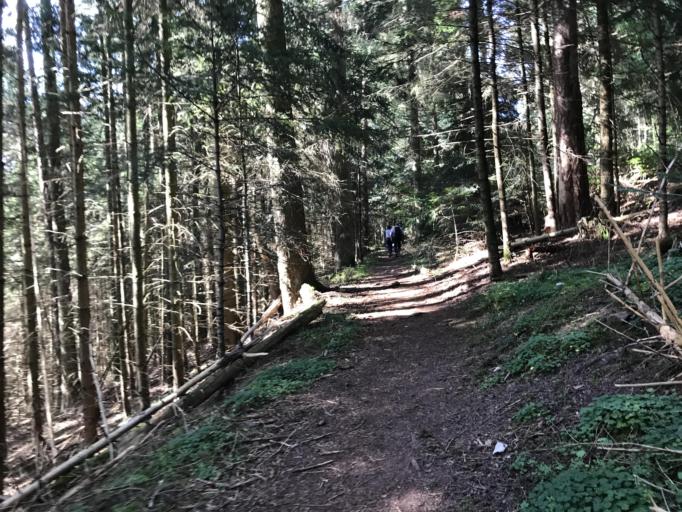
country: DE
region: Baden-Wuerttemberg
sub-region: Karlsruhe Region
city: Bad Teinach-Zavelstein
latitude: 48.7016
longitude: 8.7149
